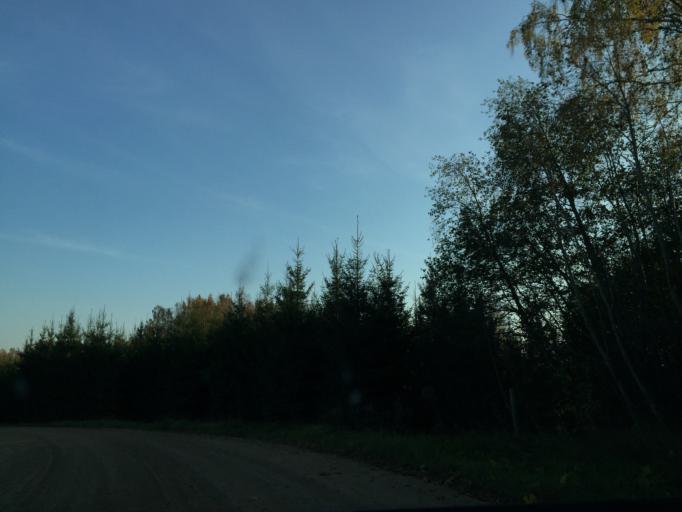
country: LV
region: Vainode
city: Vainode
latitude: 56.5991
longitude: 21.8271
